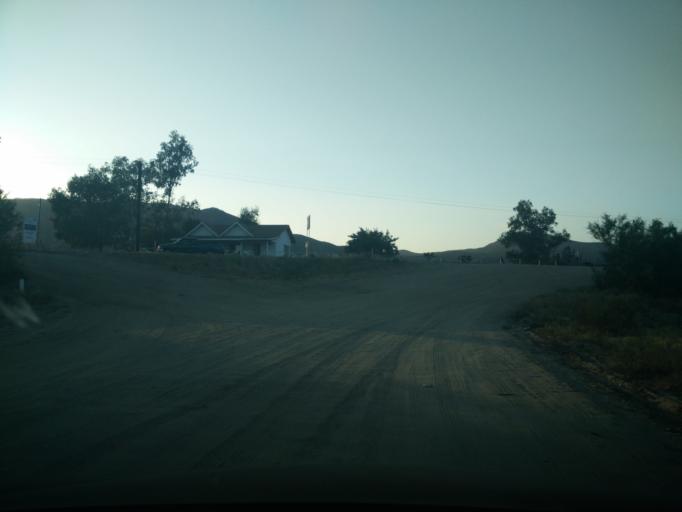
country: MX
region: Baja California
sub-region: Ensenada
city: Rancho Verde
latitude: 32.0561
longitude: -116.6479
